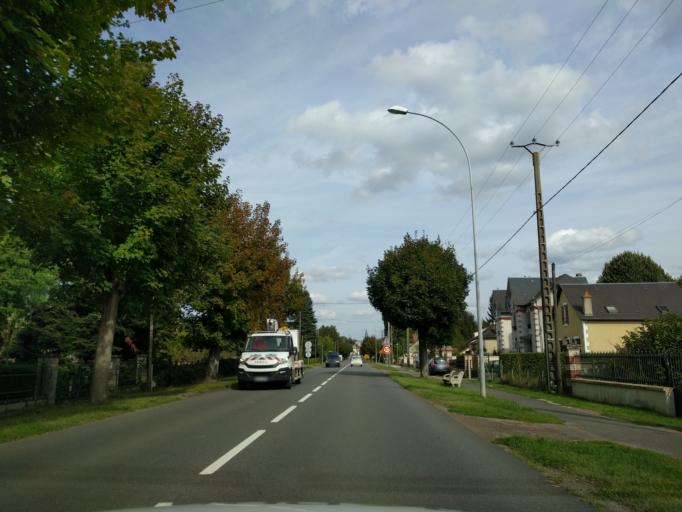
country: FR
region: Bourgogne
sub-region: Departement de la Nievre
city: La Charite-sur-Loire
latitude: 47.1726
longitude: 3.0032
